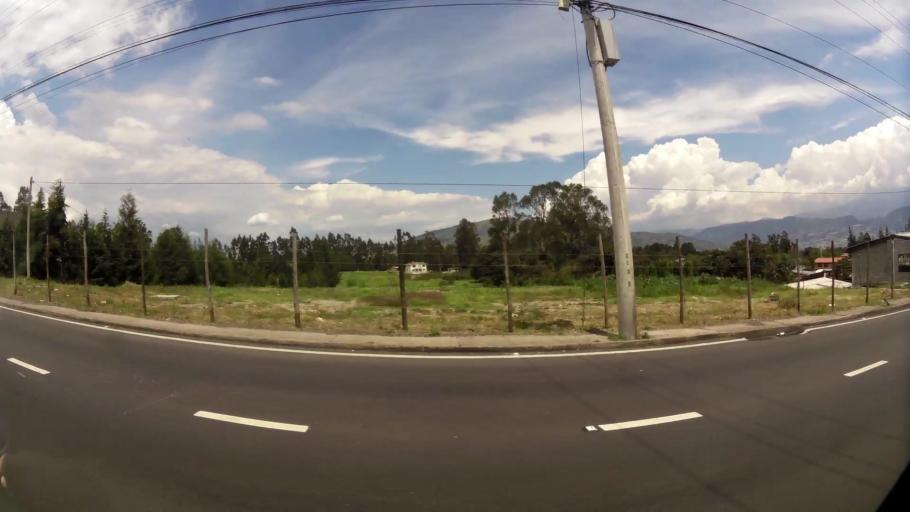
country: EC
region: Pichincha
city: Sangolqui
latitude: -0.2149
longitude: -78.3592
